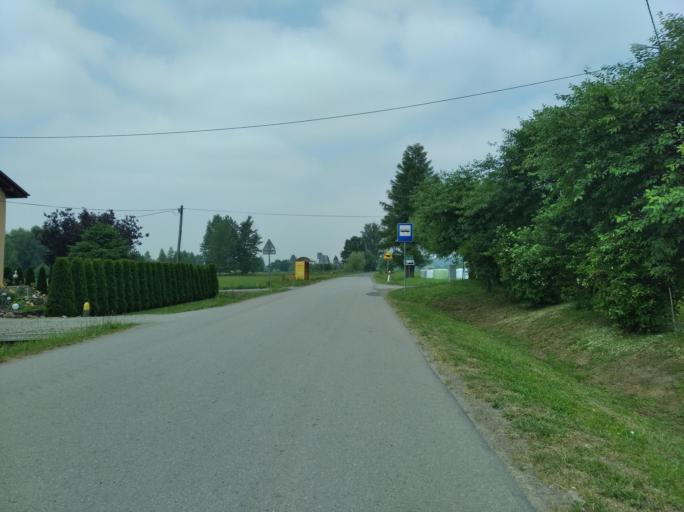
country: PL
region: Subcarpathian Voivodeship
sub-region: Powiat sanocki
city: Besko
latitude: 49.6180
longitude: 21.9423
